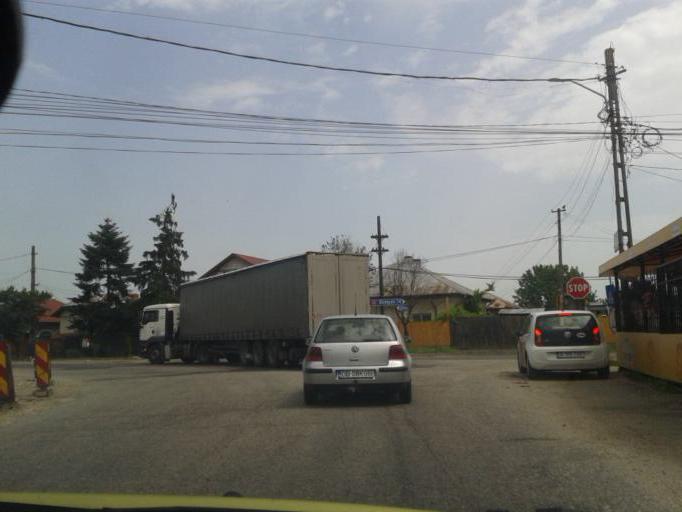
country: RO
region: Dambovita
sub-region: Comuna Petresti
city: Petresti
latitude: 44.6790
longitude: 25.3116
